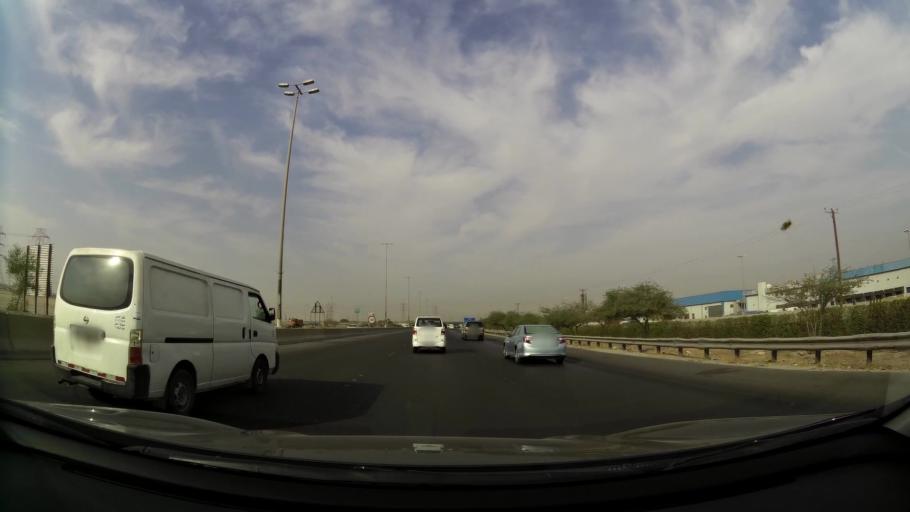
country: KW
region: Al Asimah
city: Ar Rabiyah
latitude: 29.2651
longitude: 47.8491
